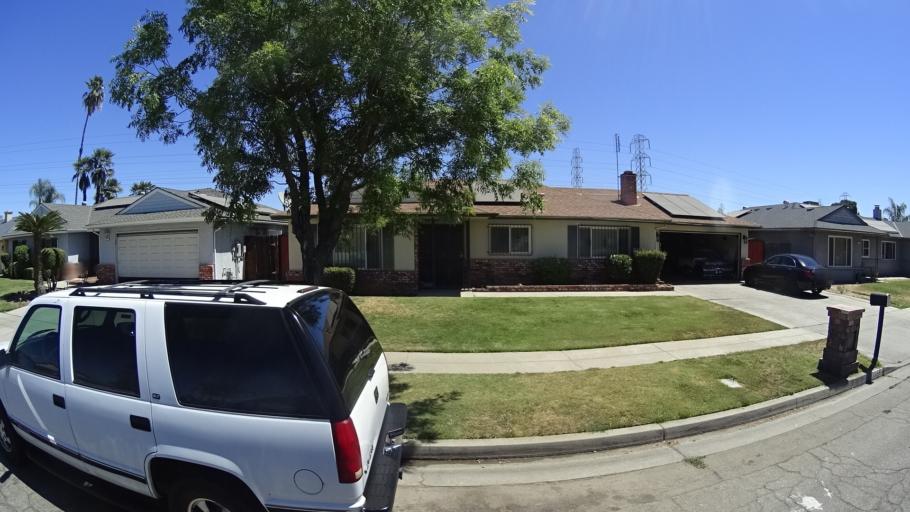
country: US
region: California
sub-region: Fresno County
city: Fresno
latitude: 36.8014
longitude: -119.8458
